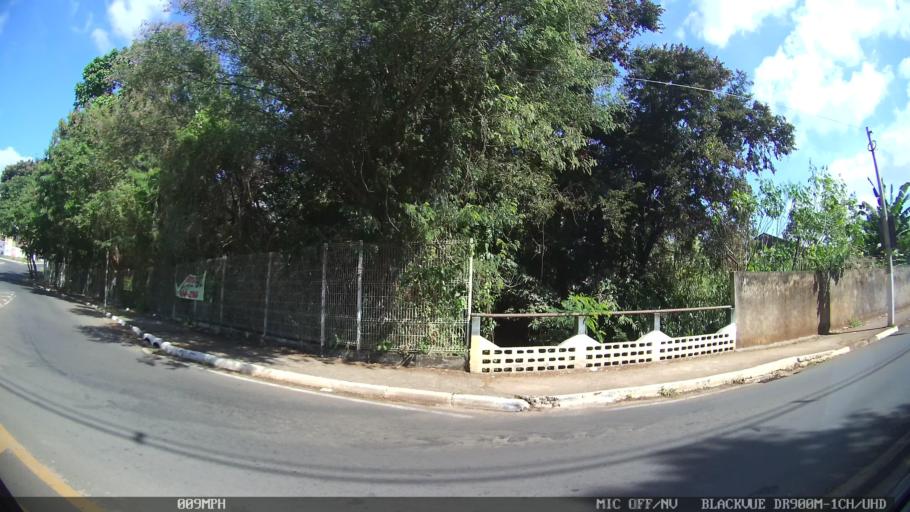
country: BR
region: Sao Paulo
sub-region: Hortolandia
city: Hortolandia
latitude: -22.8809
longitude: -47.2225
